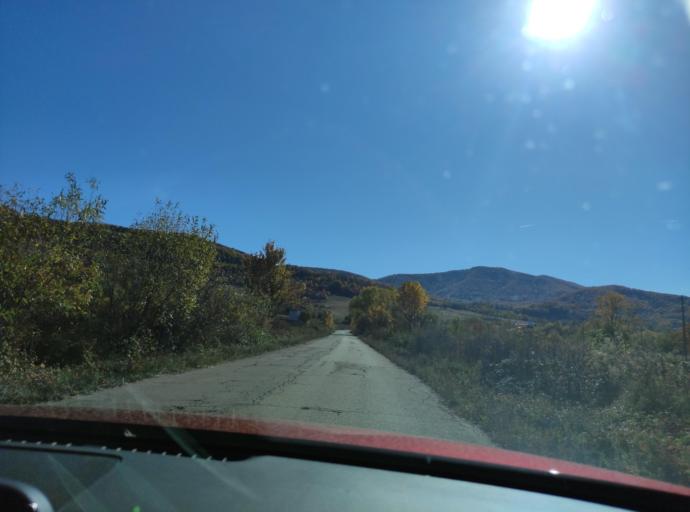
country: BG
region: Montana
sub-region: Obshtina Chiprovtsi
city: Chiprovtsi
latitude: 43.3900
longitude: 22.9220
